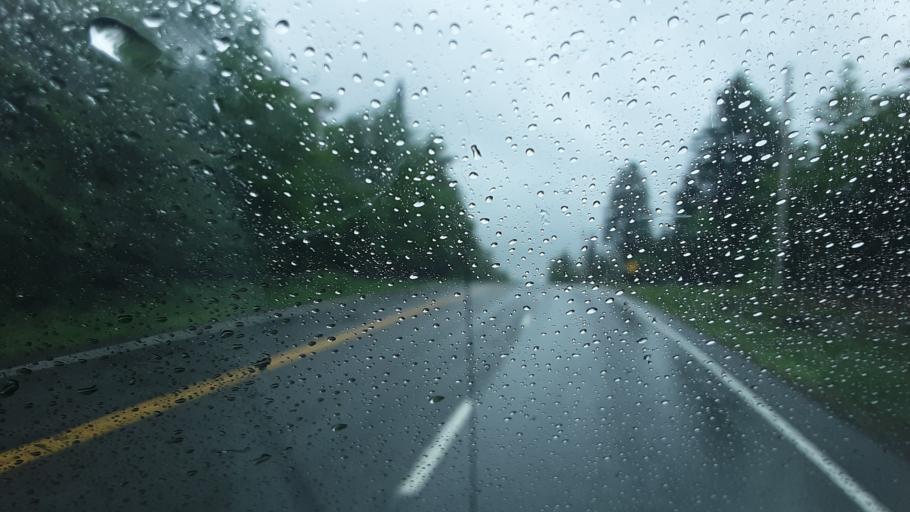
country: US
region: Maine
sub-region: Penobscot County
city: Patten
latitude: 46.1790
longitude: -68.3357
